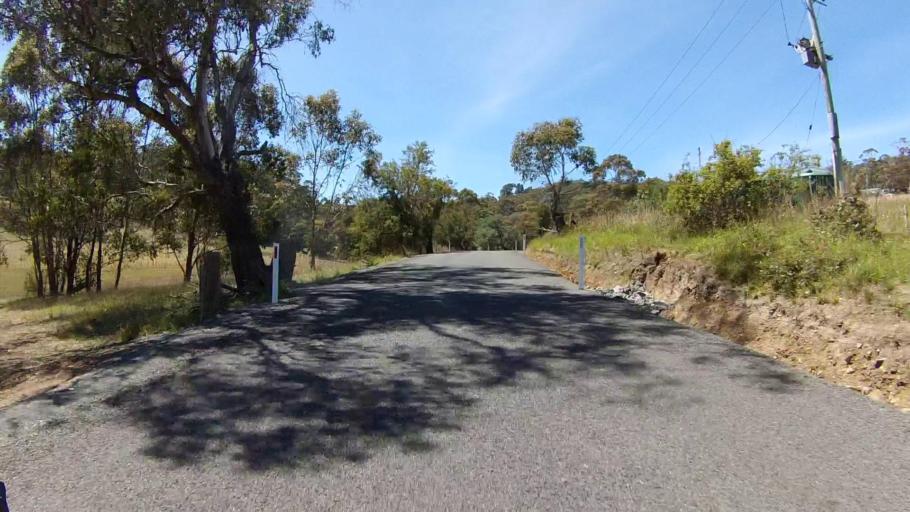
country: AU
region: Tasmania
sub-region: Clarence
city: Cambridge
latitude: -42.8524
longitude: 147.4258
